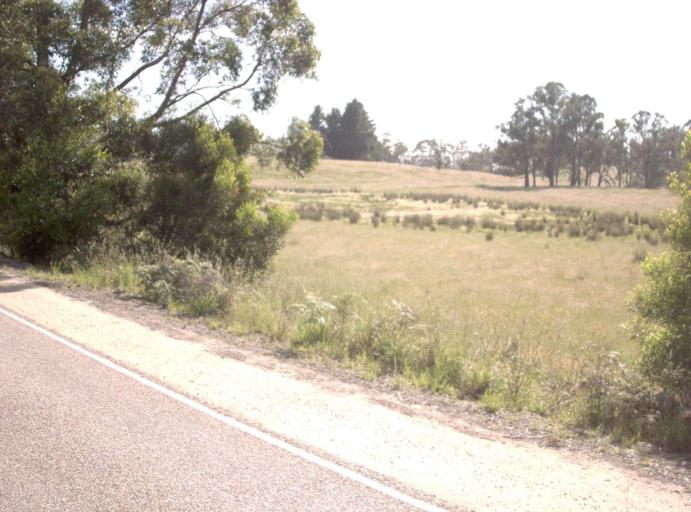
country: AU
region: Victoria
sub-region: East Gippsland
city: Lakes Entrance
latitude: -37.5315
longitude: 148.1533
